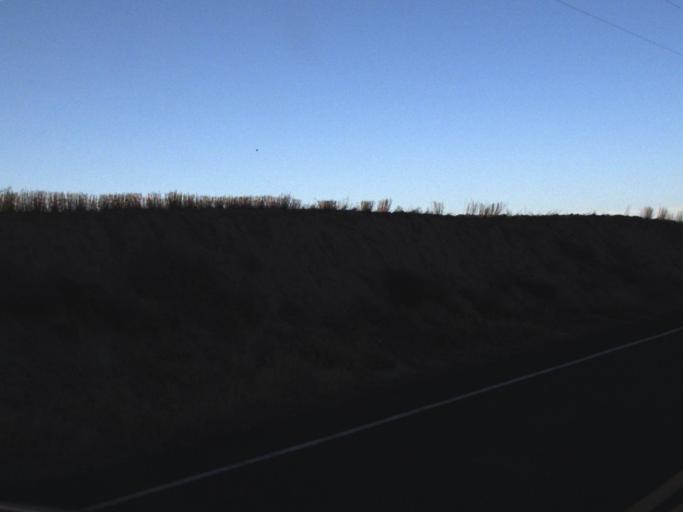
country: US
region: Washington
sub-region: Franklin County
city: Connell
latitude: 46.7491
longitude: -118.5476
